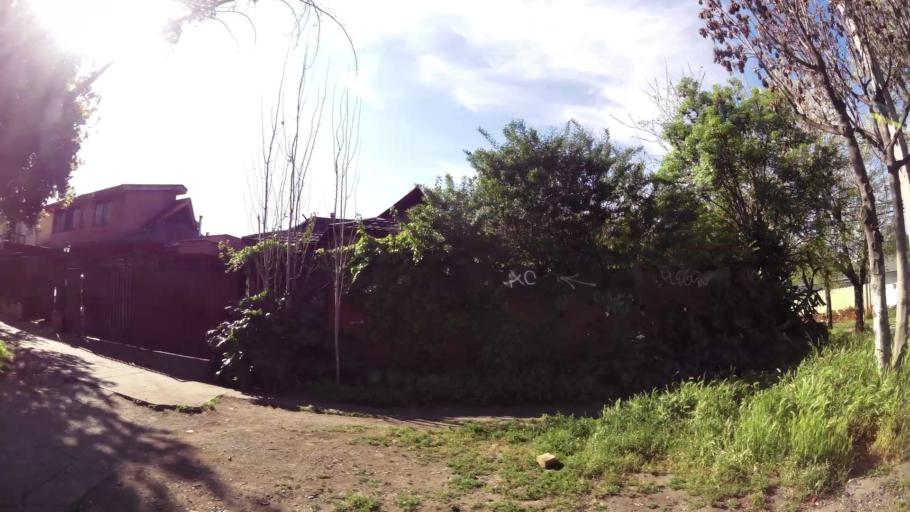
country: CL
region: Santiago Metropolitan
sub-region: Provincia de Santiago
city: Villa Presidente Frei, Nunoa, Santiago, Chile
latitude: -33.4370
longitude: -70.5611
